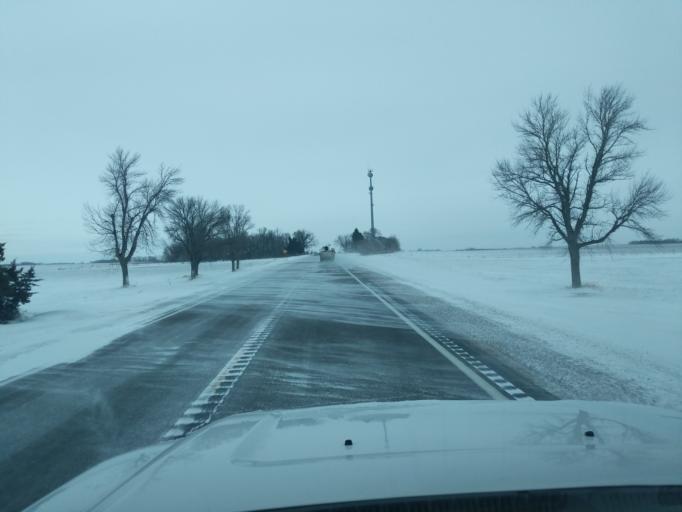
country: US
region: Minnesota
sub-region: Redwood County
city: Redwood Falls
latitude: 44.6015
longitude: -94.9944
